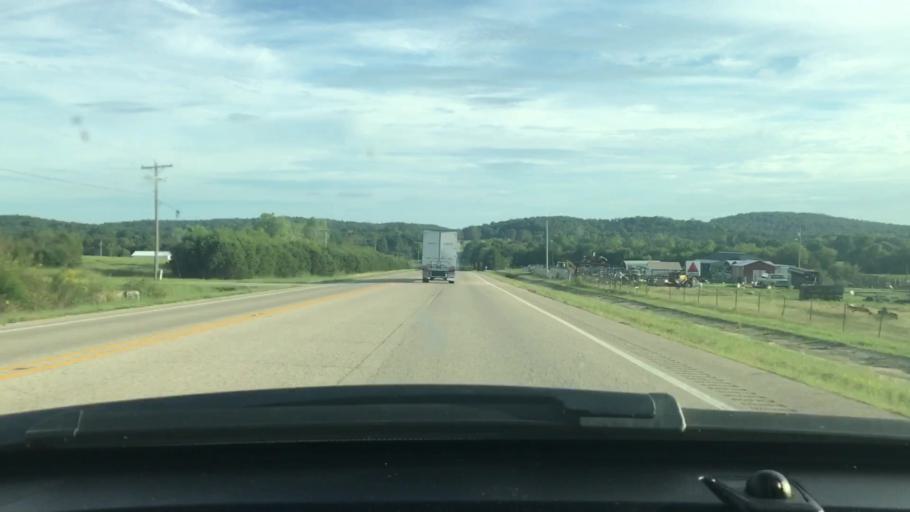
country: US
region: Arkansas
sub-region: Randolph County
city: Pocahontas
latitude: 36.1853
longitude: -91.1627
